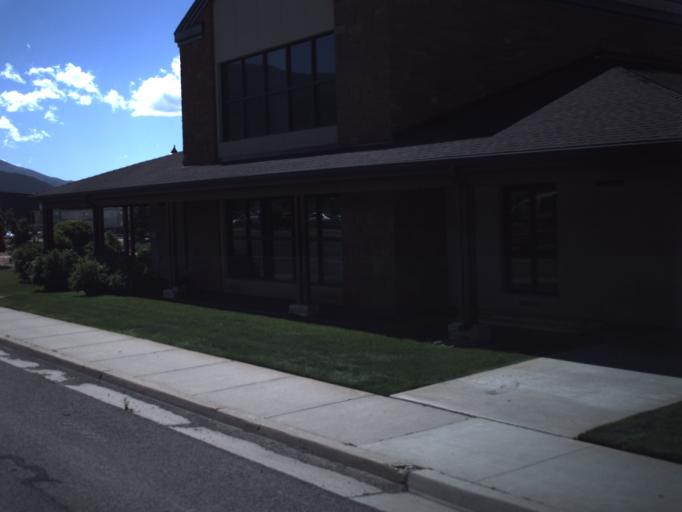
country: US
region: Utah
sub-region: Iron County
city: Cedar City
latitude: 37.6874
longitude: -113.0620
